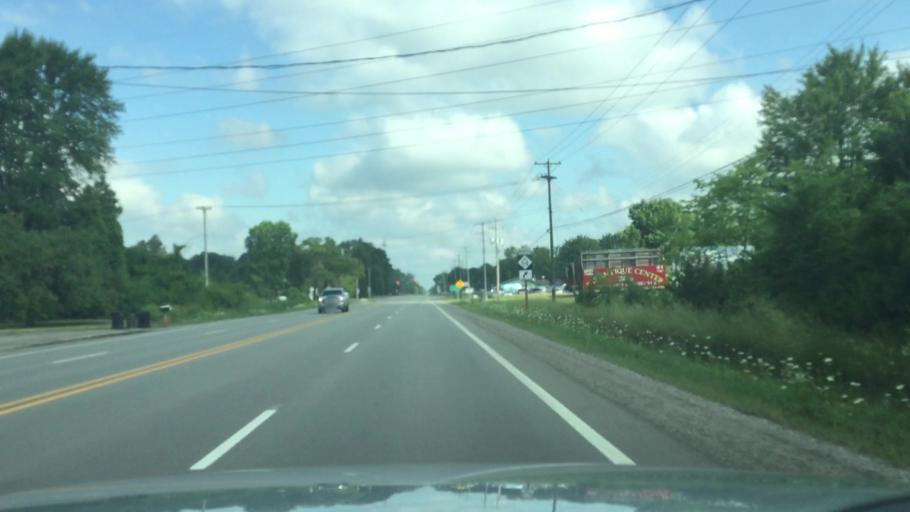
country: US
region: Michigan
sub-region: Genesee County
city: Clio
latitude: 43.2018
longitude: -83.7328
